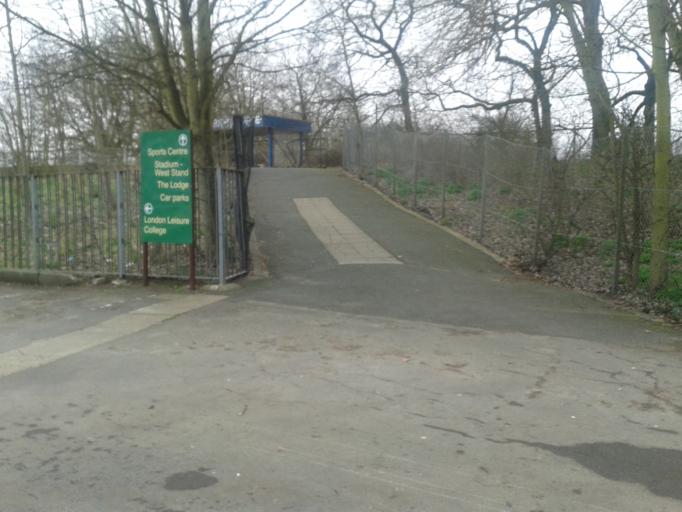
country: GB
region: England
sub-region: Greater London
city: Thornton Heath
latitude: 51.4195
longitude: -0.0671
